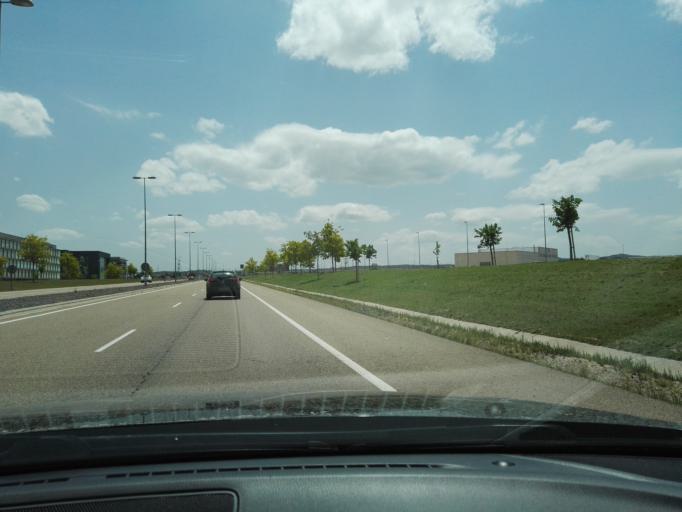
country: ES
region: Aragon
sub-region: Provincia de Zaragoza
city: Montecanal
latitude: 41.6443
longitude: -0.9950
